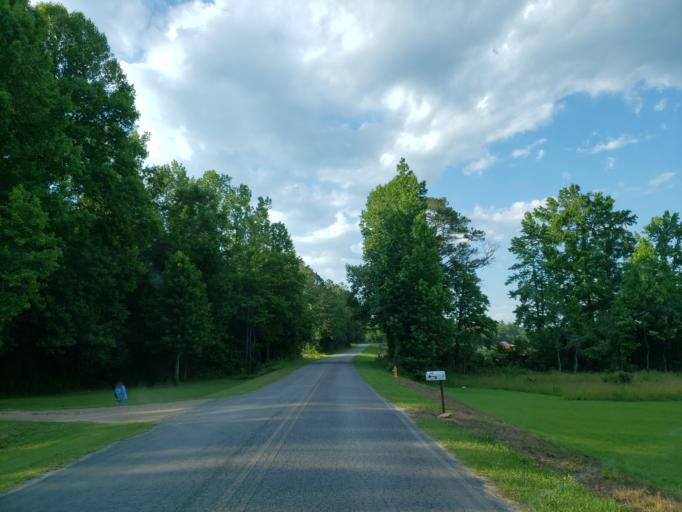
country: US
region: Georgia
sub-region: Haralson County
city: Tallapoosa
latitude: 33.8204
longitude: -85.2846
